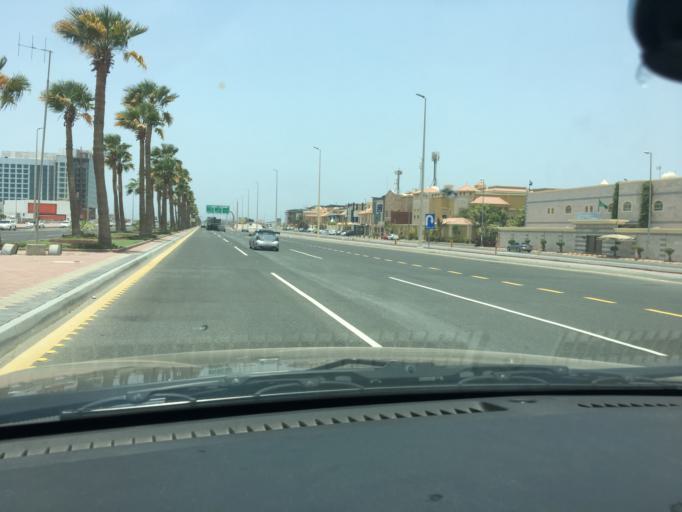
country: SA
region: Makkah
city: Jeddah
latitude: 21.6700
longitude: 39.1260
